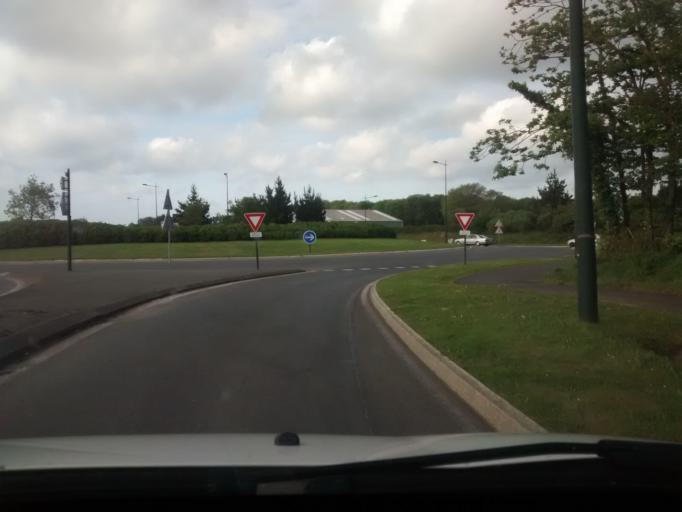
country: FR
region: Brittany
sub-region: Departement des Cotes-d'Armor
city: Saint-Quay-Perros
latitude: 48.7656
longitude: -3.4495
